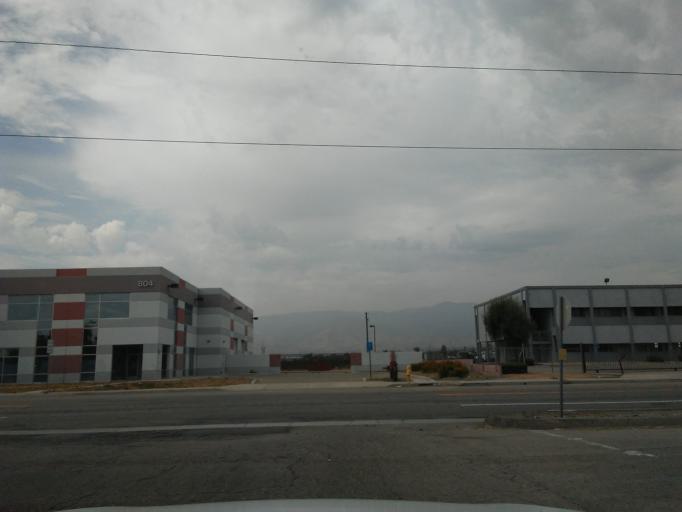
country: US
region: California
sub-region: San Bernardino County
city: San Bernardino
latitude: 34.0919
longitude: -117.2693
